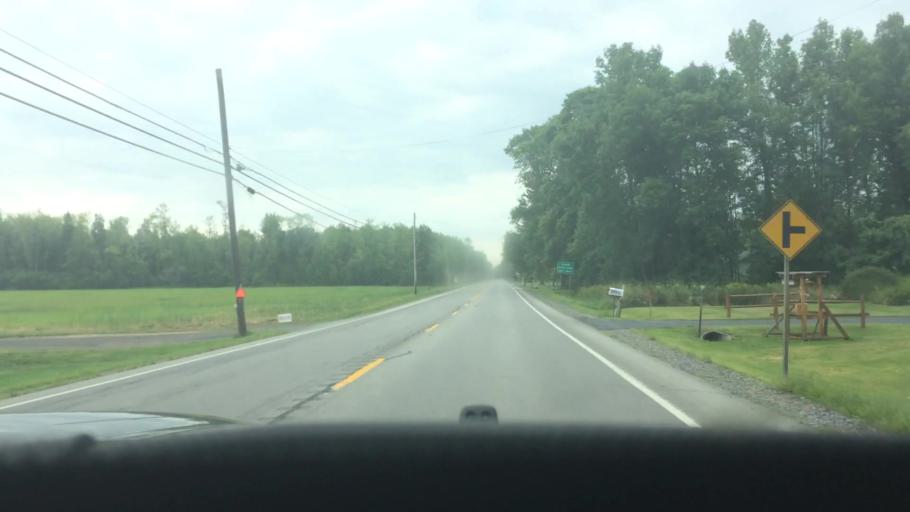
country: US
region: New York
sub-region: St. Lawrence County
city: Ogdensburg
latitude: 44.6544
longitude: -75.4468
